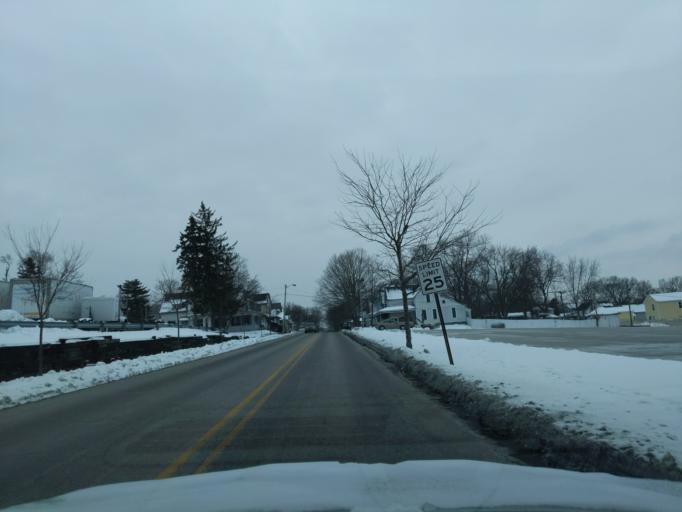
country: US
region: Indiana
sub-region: Tippecanoe County
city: Lafayette
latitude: 40.4296
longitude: -86.8872
